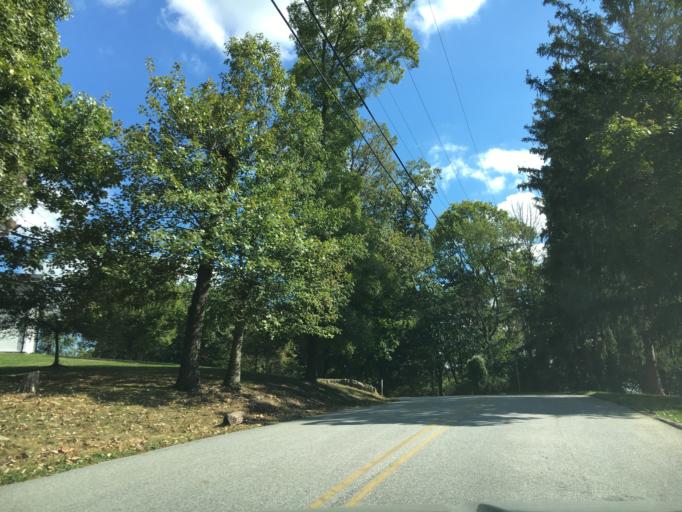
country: US
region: Pennsylvania
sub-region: York County
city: East York
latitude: 40.0042
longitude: -76.6781
